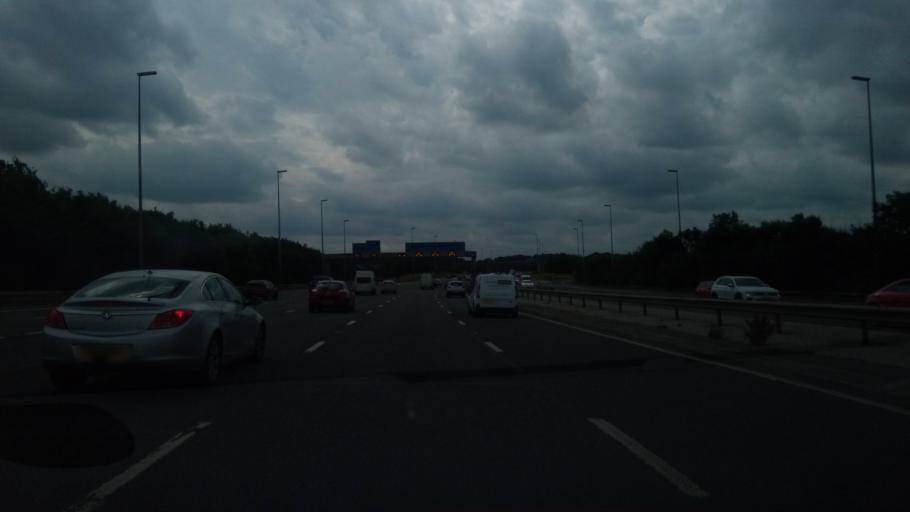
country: GB
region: England
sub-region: Lancashire
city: Goosnargh
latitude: 53.7700
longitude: -2.6375
